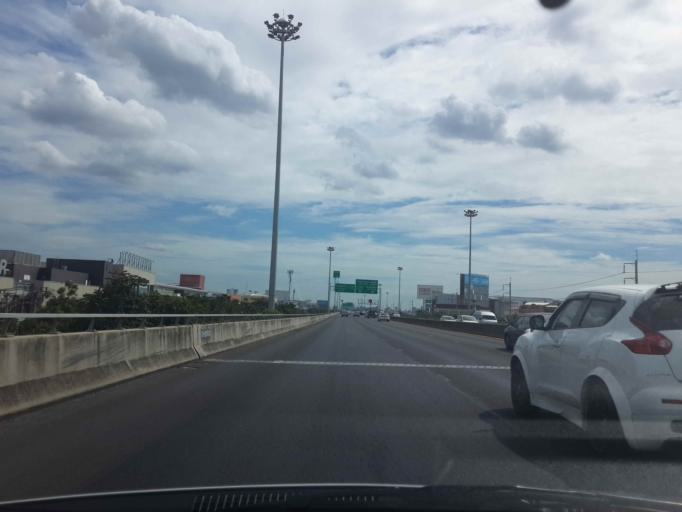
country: TH
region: Bangkok
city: Lat Phrao
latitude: 13.8063
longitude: 100.6178
